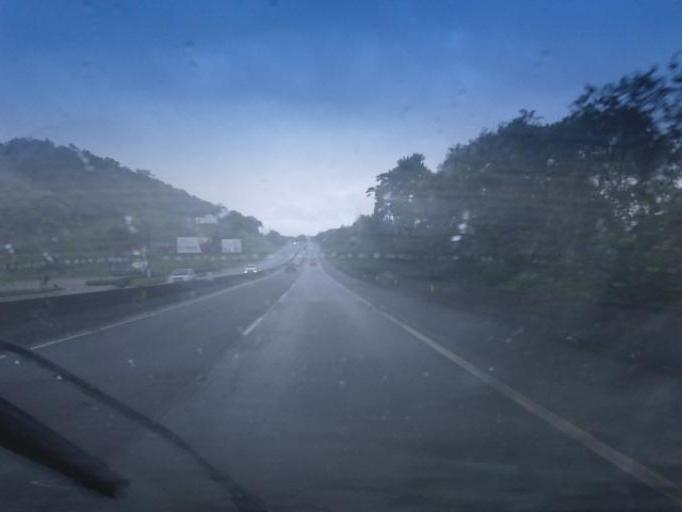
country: BR
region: Santa Catarina
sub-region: Barra Velha
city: Barra Velha
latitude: -26.7067
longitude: -48.7013
